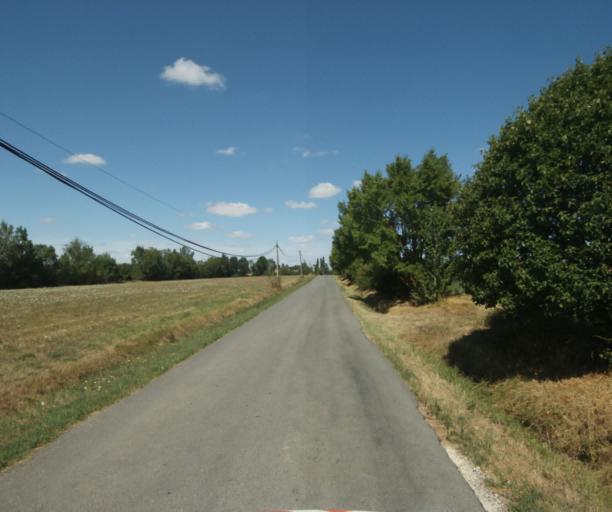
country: FR
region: Midi-Pyrenees
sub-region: Departement de la Haute-Garonne
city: Revel
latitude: 43.4861
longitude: 2.0144
